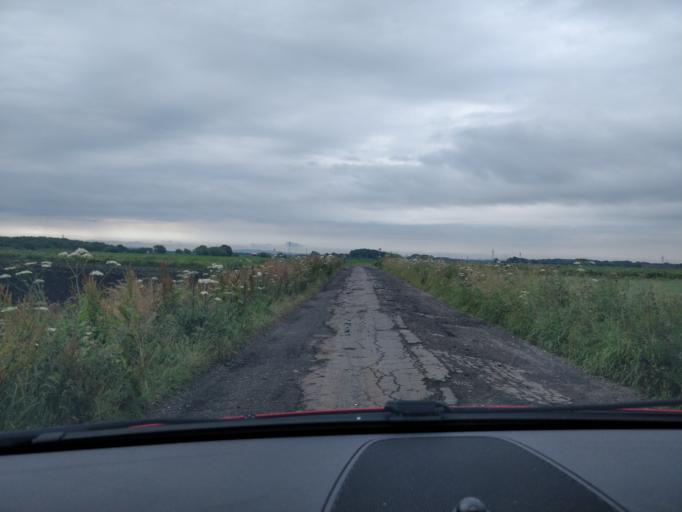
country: GB
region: England
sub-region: Lancashire
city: Banks
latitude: 53.6623
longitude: -2.9336
